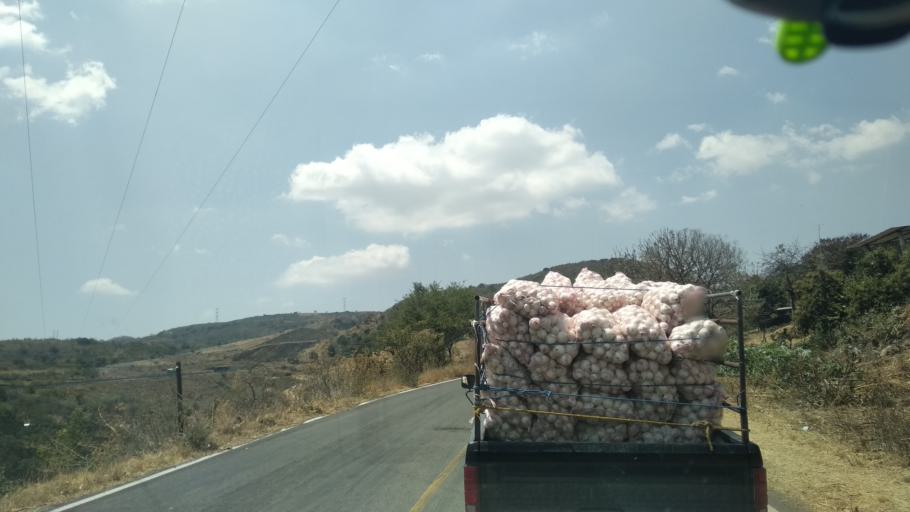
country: MX
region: Puebla
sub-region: Atzitzihuacan
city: Santiago Atzitzihuacan
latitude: 18.8345
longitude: -98.5978
